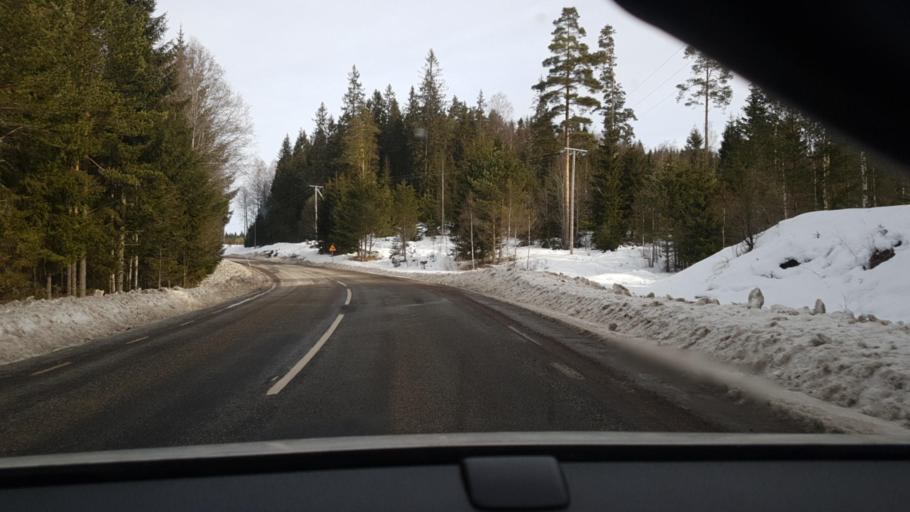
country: SE
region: Vaermland
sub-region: Arjangs Kommun
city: Arjaeng
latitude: 59.5671
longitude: 12.2044
